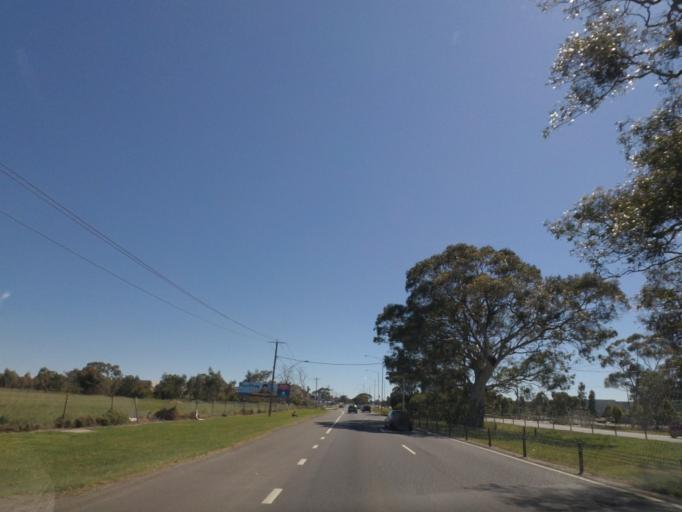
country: AU
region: Victoria
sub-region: Hume
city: Craigieburn
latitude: -37.6190
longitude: 144.9473
